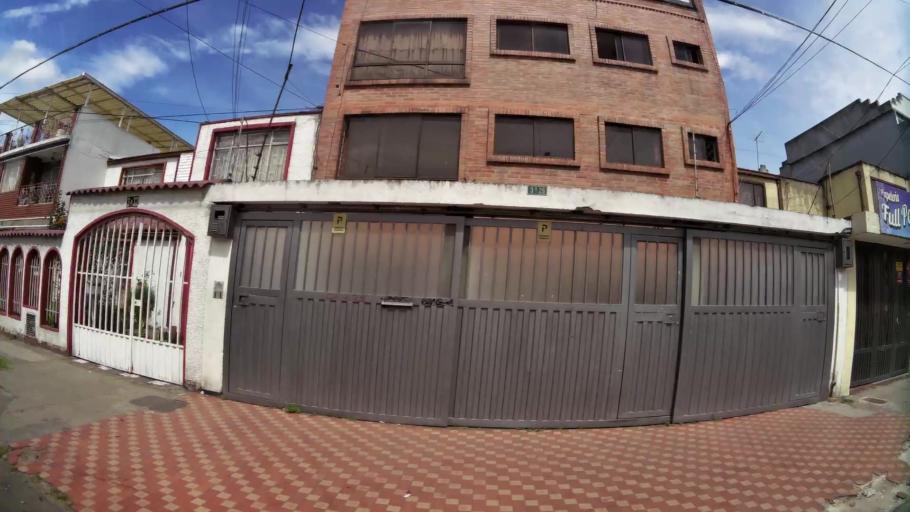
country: CO
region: Bogota D.C.
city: Bogota
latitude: 4.6261
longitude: -74.1337
